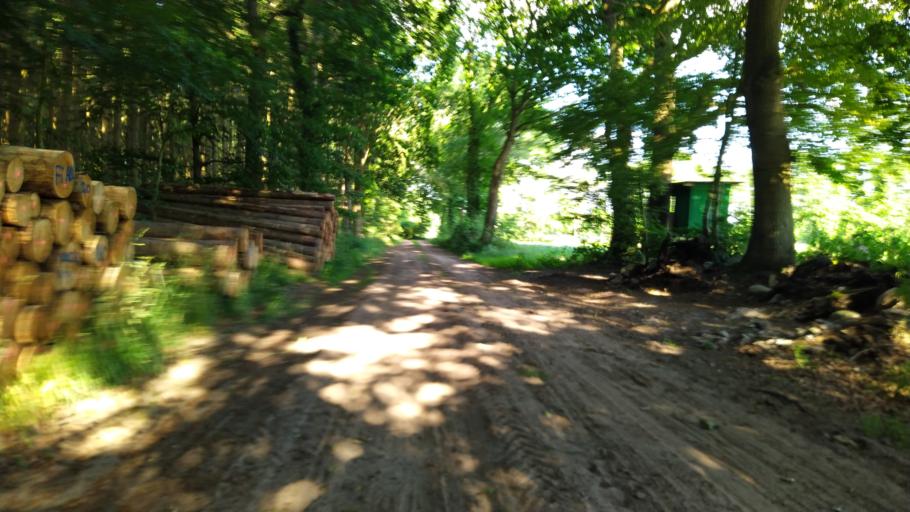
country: DE
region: Lower Saxony
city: Lintig
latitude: 53.5977
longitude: 8.9146
